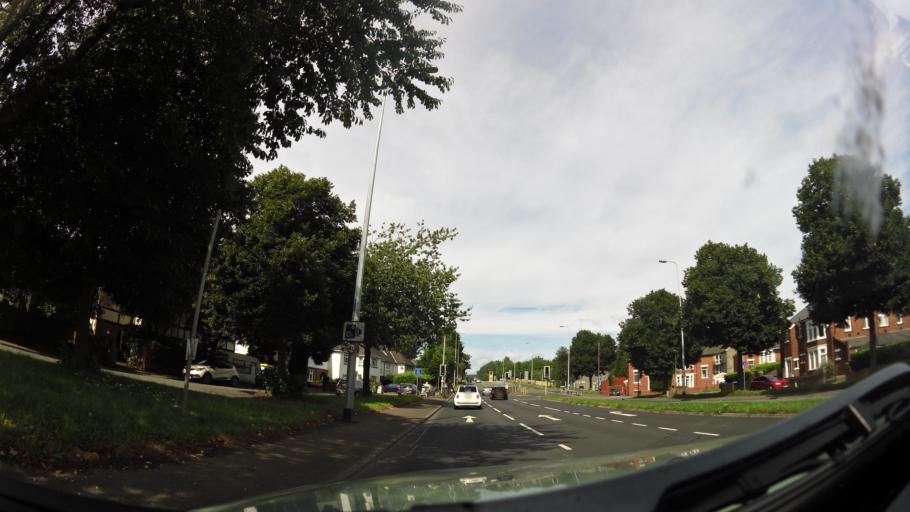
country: GB
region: Wales
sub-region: Cardiff
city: Radyr
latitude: 51.5193
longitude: -3.2217
